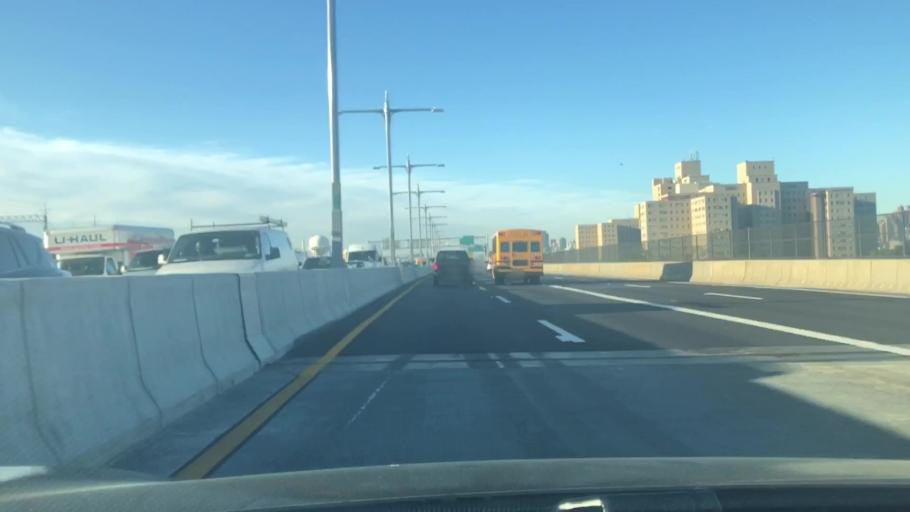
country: US
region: New York
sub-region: New York County
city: Manhattan
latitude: 40.7925
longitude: -73.9244
